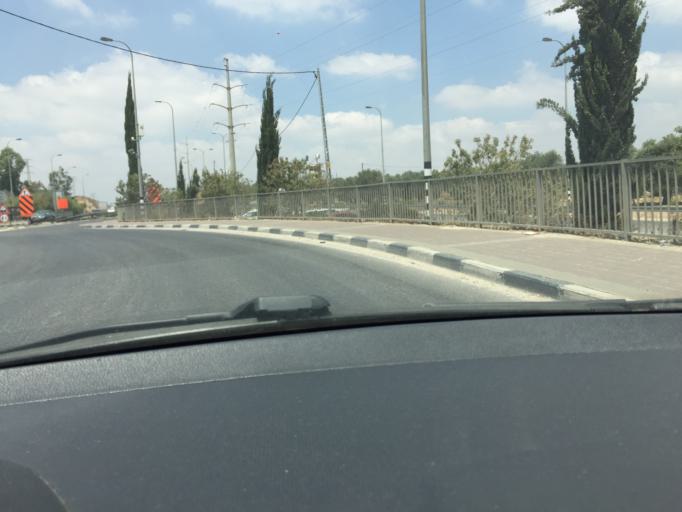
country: PS
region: West Bank
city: Kifil Haris
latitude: 32.1097
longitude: 35.1656
